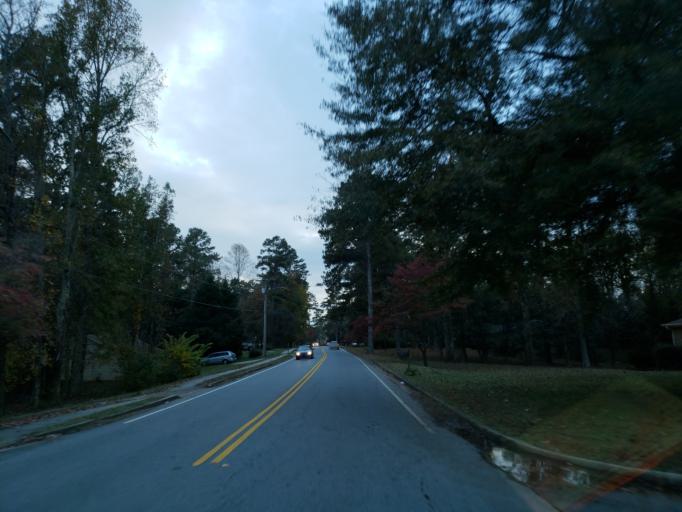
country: US
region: Georgia
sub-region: Cobb County
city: Kennesaw
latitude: 34.0253
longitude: -84.6524
